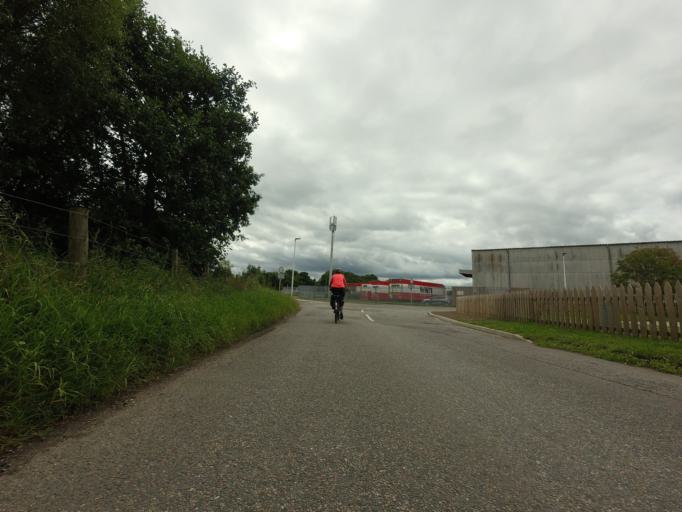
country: GB
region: Scotland
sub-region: Moray
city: Forres
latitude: 57.6129
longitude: -3.6193
